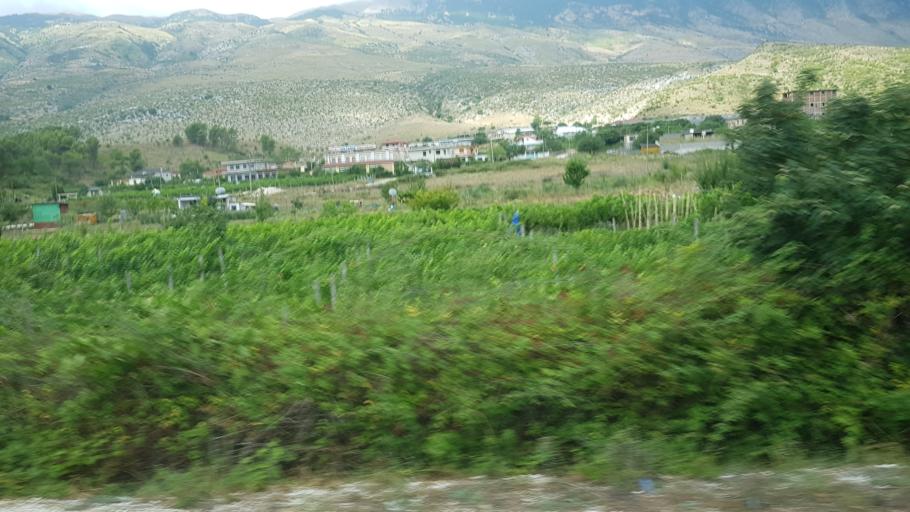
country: AL
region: Gjirokaster
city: Gjirokaster
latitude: 40.1041
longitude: 20.1236
